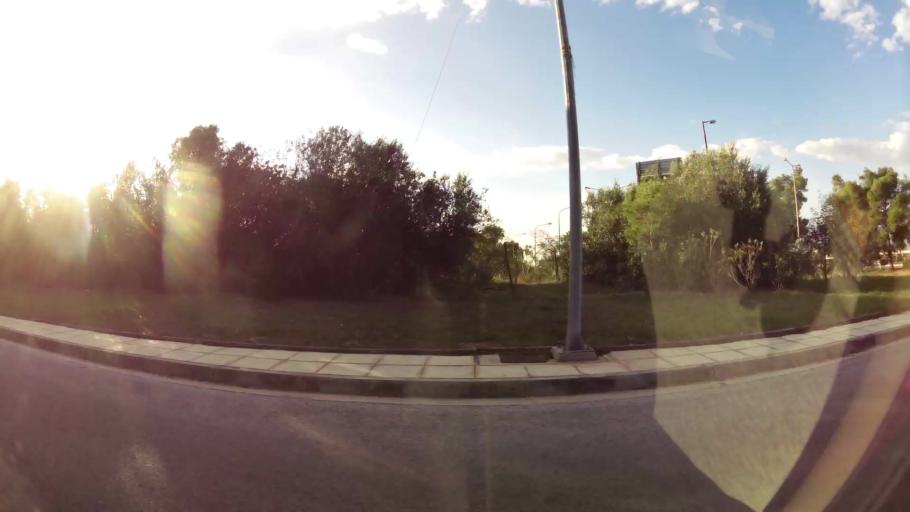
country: GR
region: Attica
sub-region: Nomarchia Athinas
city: Elliniko
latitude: 37.8872
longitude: 23.7432
